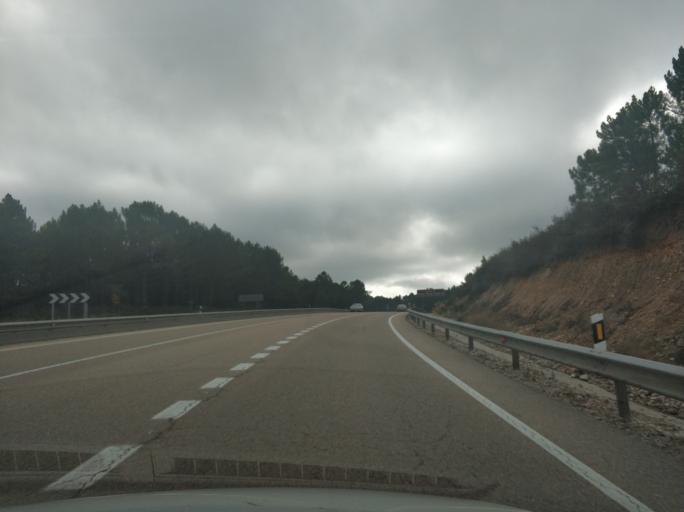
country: ES
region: Castille and Leon
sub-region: Provincia de Soria
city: Muriel Viejo
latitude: 41.8272
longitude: -2.9458
